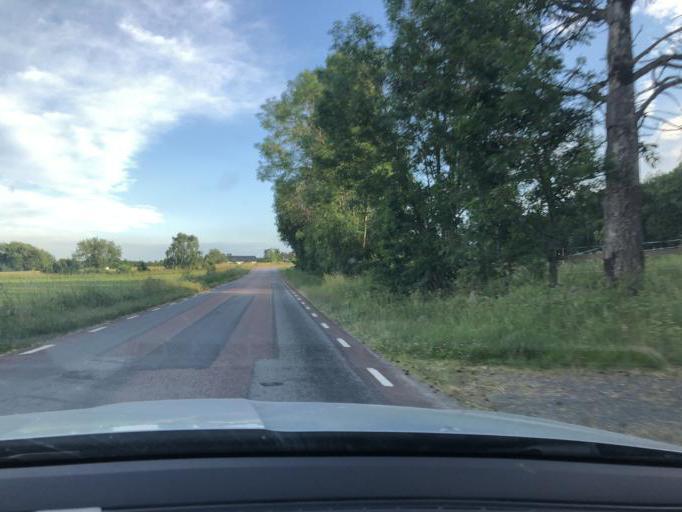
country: SE
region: Blekinge
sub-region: Solvesborgs Kommun
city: Soelvesborg
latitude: 56.1377
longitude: 14.6077
